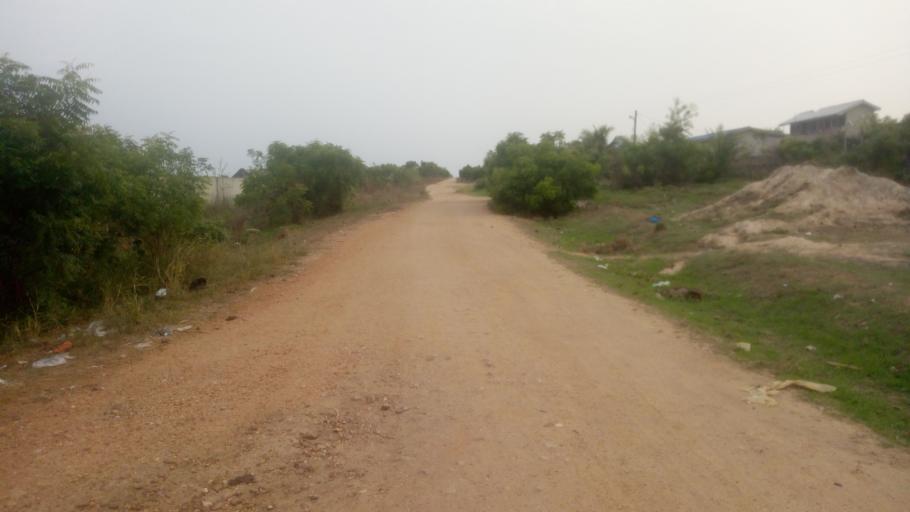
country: GH
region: Central
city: Winneba
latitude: 5.3774
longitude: -0.6288
